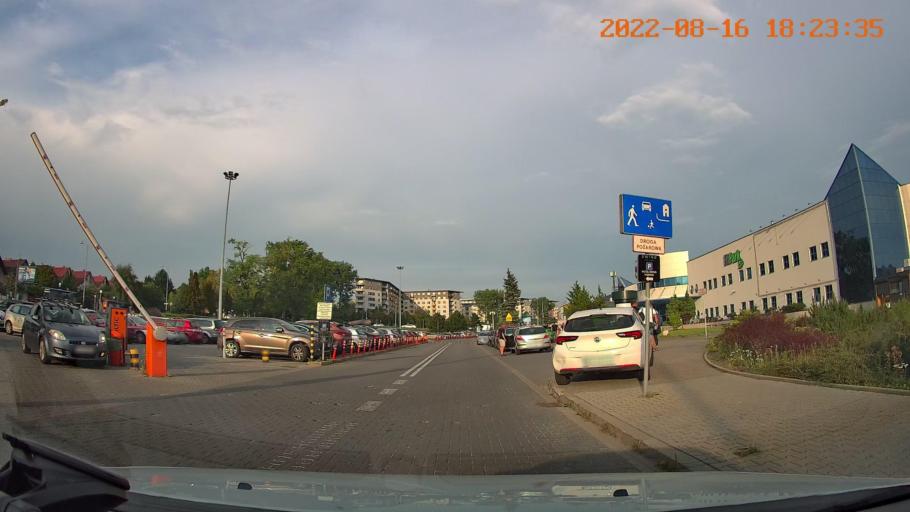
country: PL
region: Lesser Poland Voivodeship
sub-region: Krakow
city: Krakow
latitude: 50.0894
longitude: 19.9818
